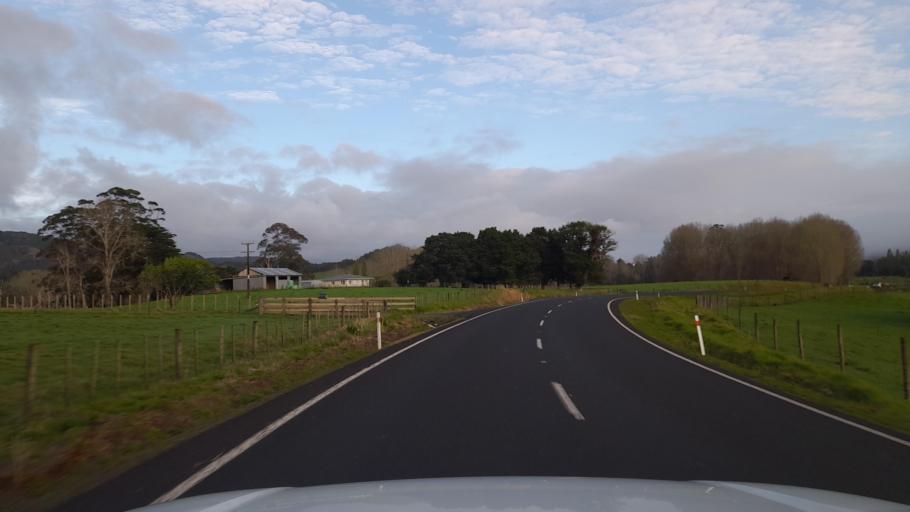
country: NZ
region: Northland
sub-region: Kaipara District
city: Dargaville
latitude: -35.6679
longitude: 173.8856
